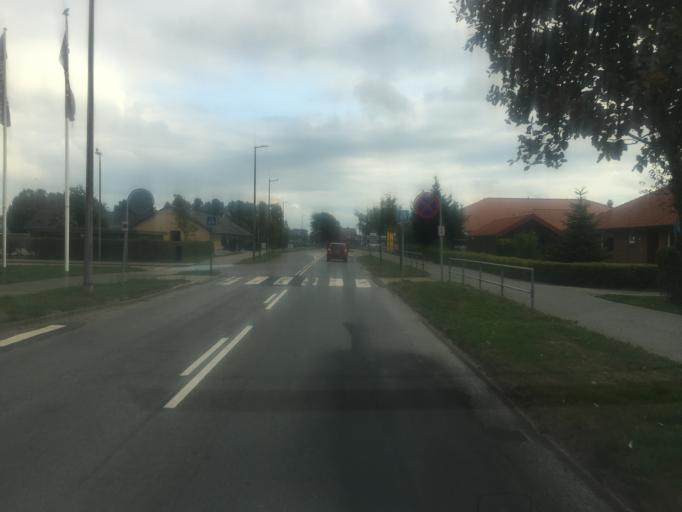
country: DK
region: South Denmark
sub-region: Tonder Kommune
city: Tonder
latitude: 54.9409
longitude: 8.8557
